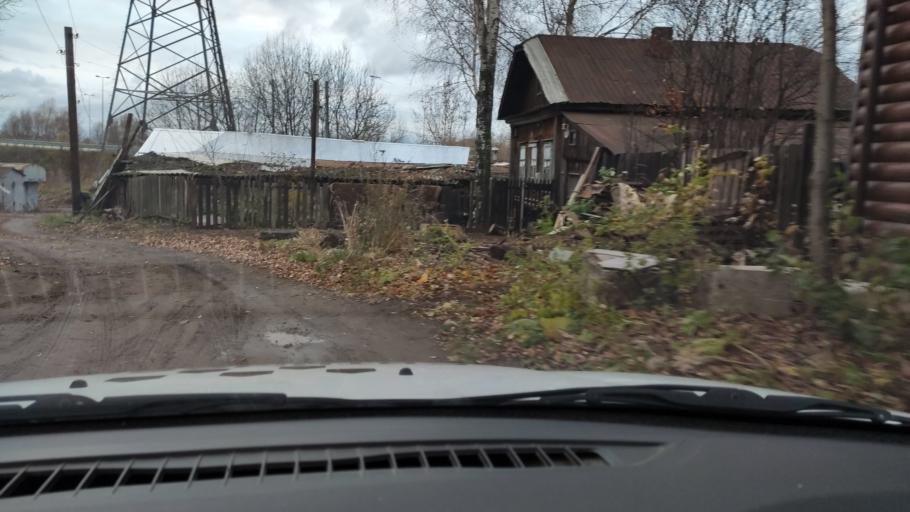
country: RU
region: Perm
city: Kondratovo
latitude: 57.9995
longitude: 56.1311
